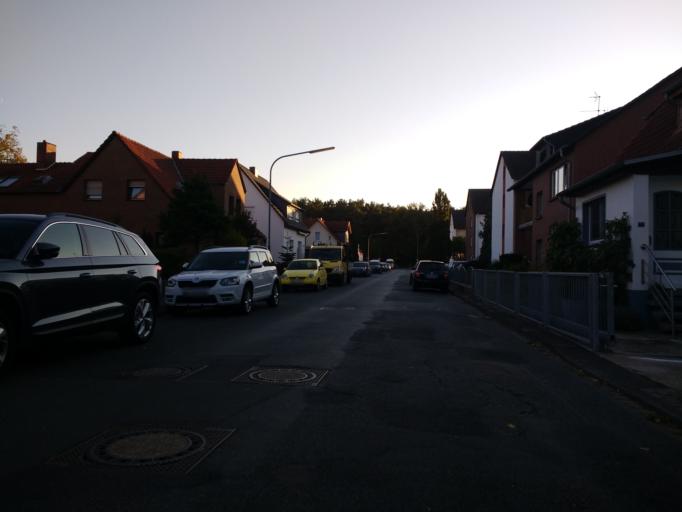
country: DE
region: Lower Saxony
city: Gifhorn
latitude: 52.4829
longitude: 10.5549
